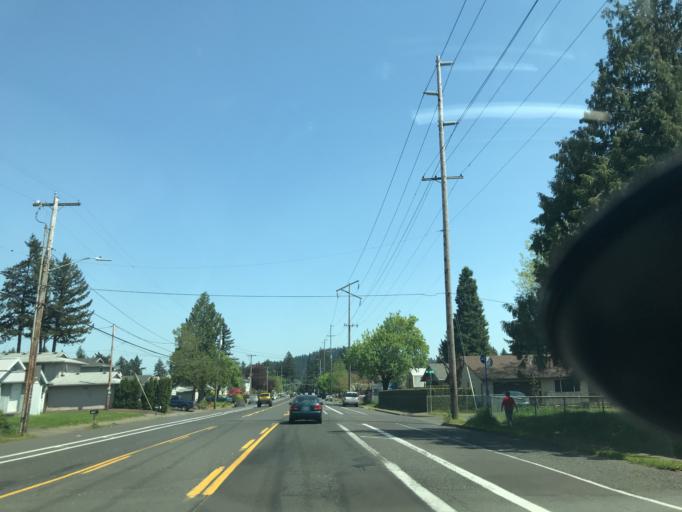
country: US
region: Oregon
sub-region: Multnomah County
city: Lents
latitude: 45.4897
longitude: -122.5425
